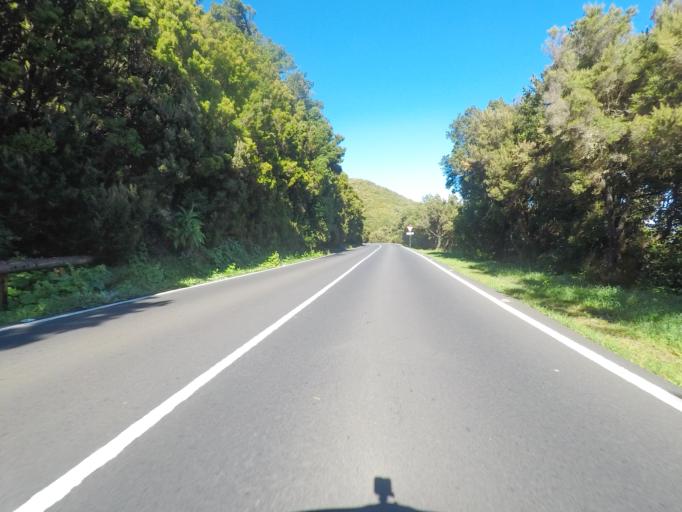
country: ES
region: Canary Islands
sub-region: Provincia de Santa Cruz de Tenerife
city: Alajero
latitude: 28.1079
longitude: -17.2401
